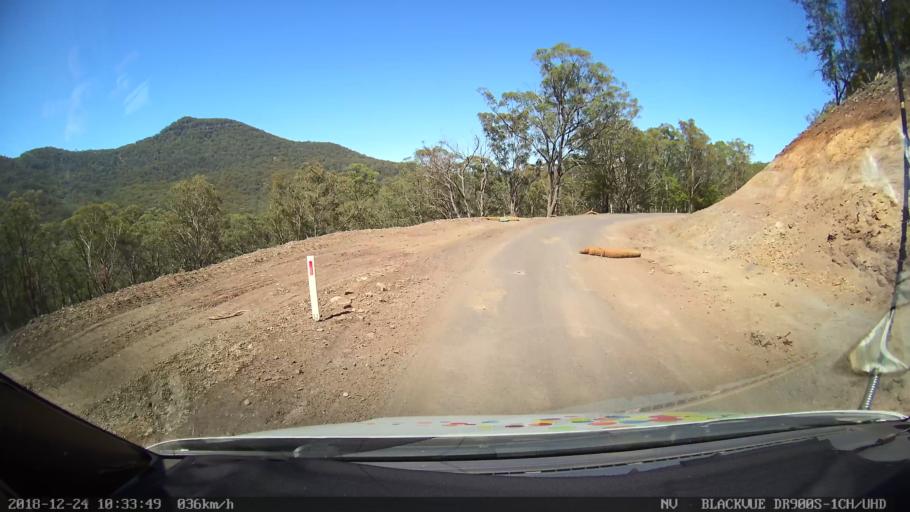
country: AU
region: New South Wales
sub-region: Upper Hunter Shire
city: Merriwa
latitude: -31.8434
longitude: 150.5089
